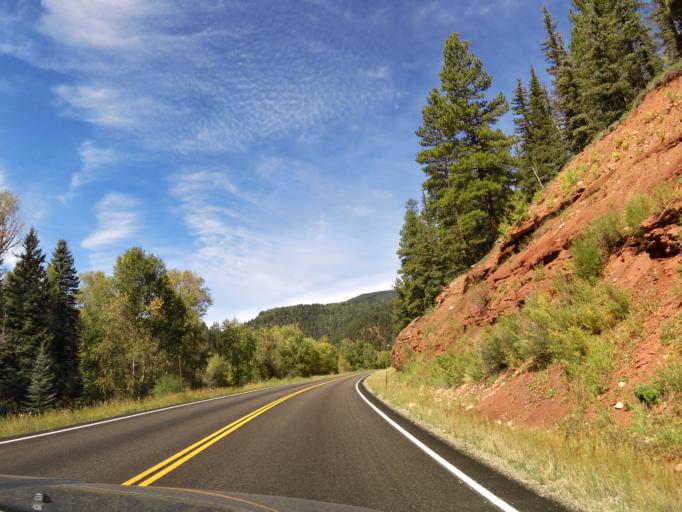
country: US
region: Colorado
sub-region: Montezuma County
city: Mancos
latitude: 37.5920
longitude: -108.1263
